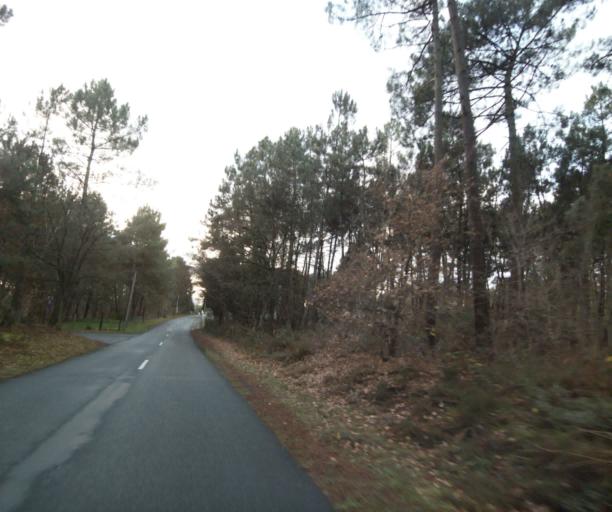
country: FR
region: Pays de la Loire
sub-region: Departement de la Sarthe
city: Ruaudin
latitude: 47.9636
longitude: 0.2275
